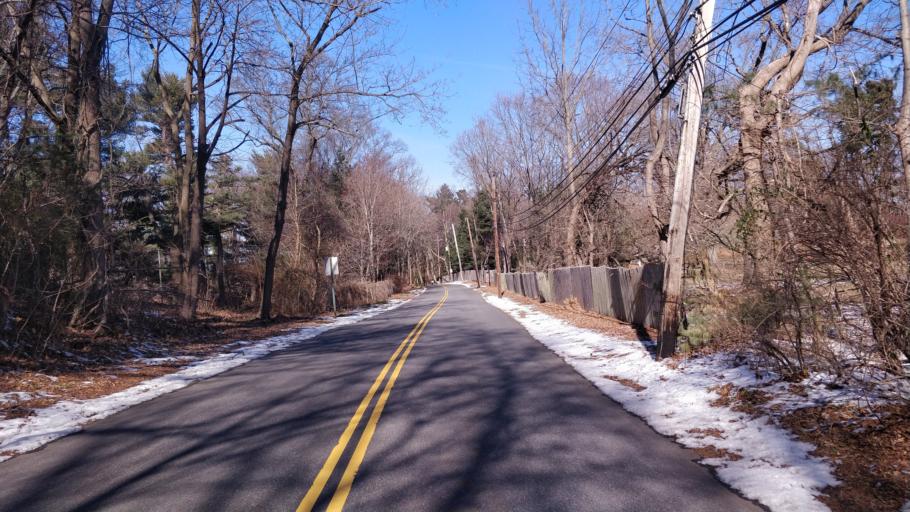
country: US
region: New York
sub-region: Nassau County
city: Westbury
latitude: 40.7740
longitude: -73.5856
